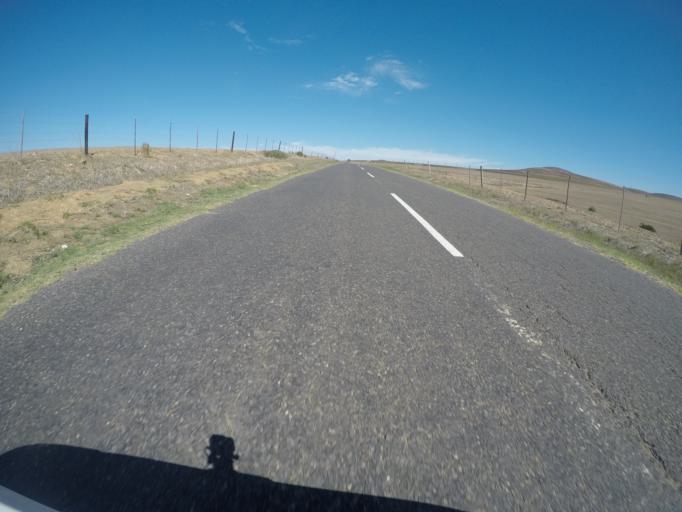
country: ZA
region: Western Cape
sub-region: City of Cape Town
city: Atlantis
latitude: -33.7014
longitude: 18.5878
